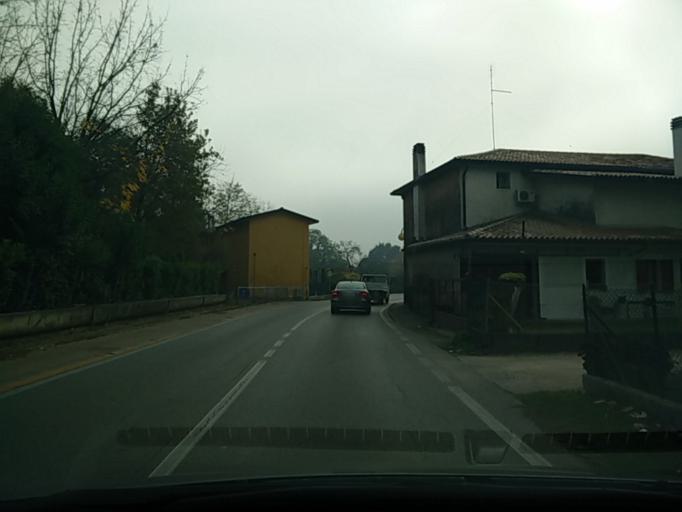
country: IT
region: Veneto
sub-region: Provincia di Treviso
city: Padernello
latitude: 45.6879
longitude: 12.1254
